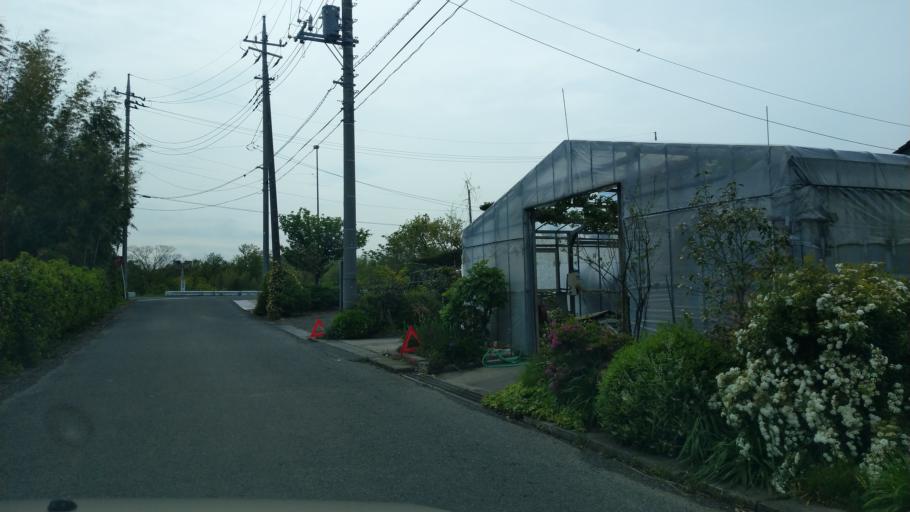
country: JP
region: Saitama
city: Kasukabe
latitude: 35.9433
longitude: 139.7282
